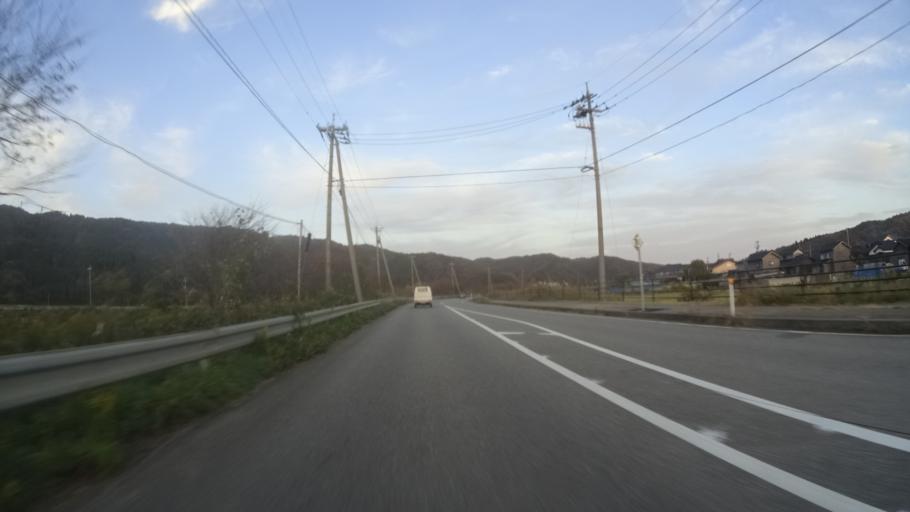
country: JP
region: Ishikawa
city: Nanao
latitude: 37.2907
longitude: 136.7423
